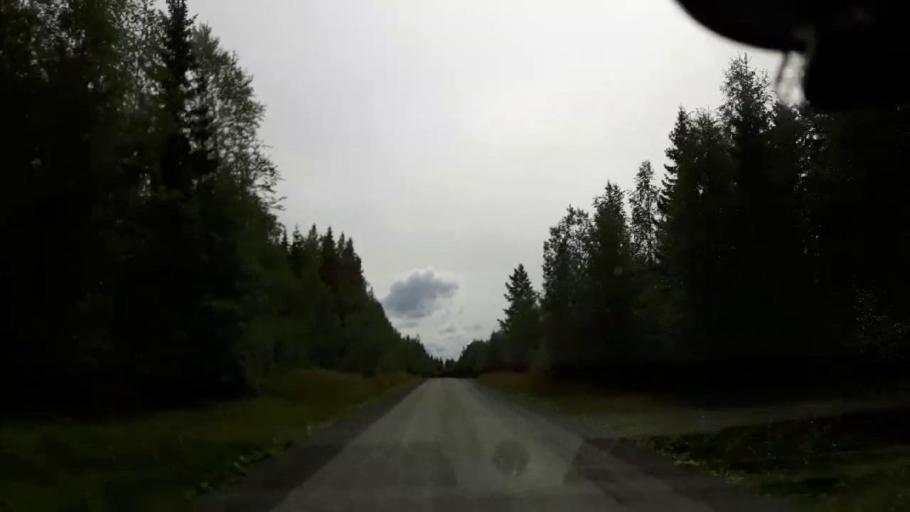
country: SE
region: Jaemtland
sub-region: Krokoms Kommun
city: Valla
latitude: 63.6348
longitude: 14.0174
